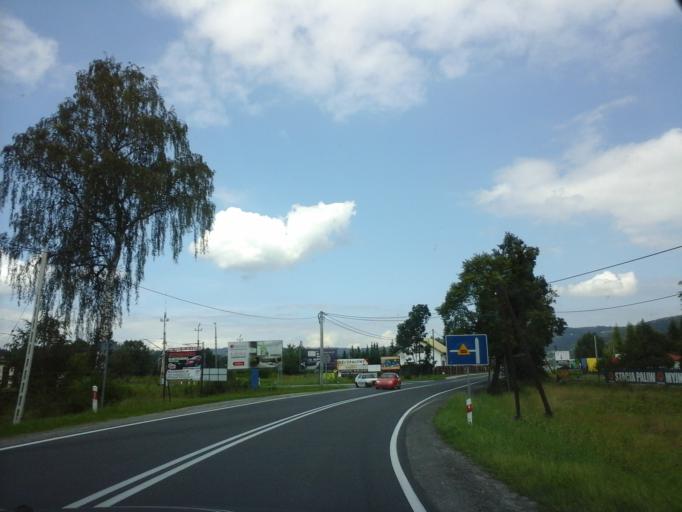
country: PL
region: Lesser Poland Voivodeship
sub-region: Powiat suski
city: Juszczyn
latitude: 49.7096
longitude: 19.6892
